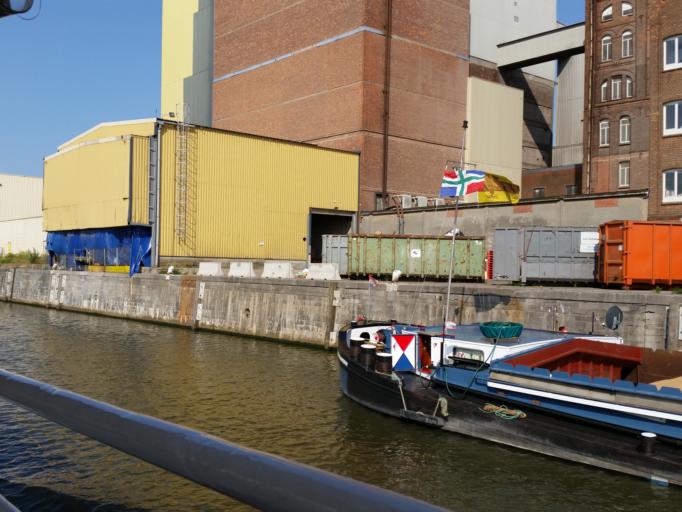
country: BE
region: Flanders
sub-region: Provincie Vlaams-Brabant
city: Diegem
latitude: 50.8958
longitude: 4.4010
